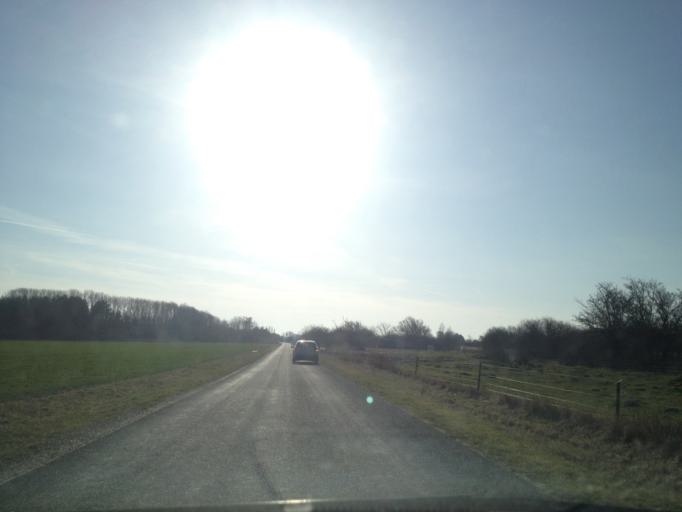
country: DK
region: South Denmark
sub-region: Kerteminde Kommune
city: Kerteminde
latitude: 55.5484
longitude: 10.6288
